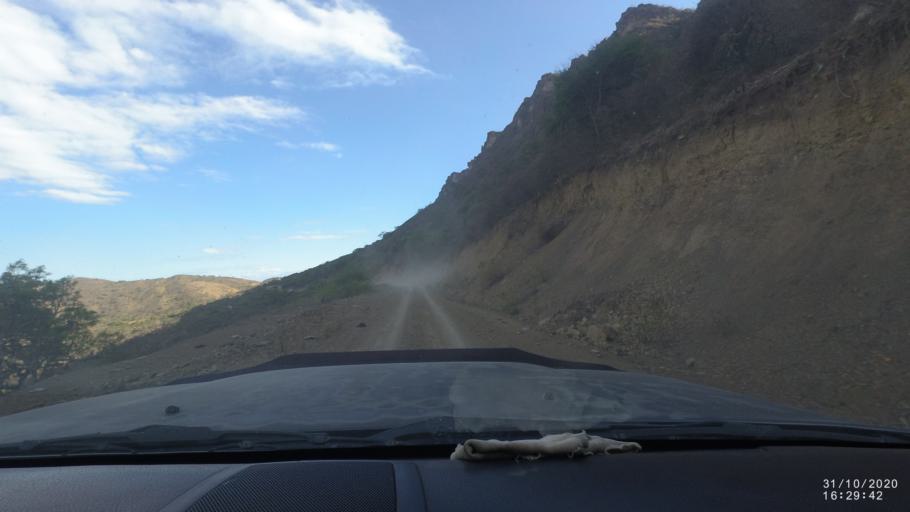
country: BO
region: Chuquisaca
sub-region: Provincia Zudanez
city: Mojocoya
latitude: -18.4217
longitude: -64.5851
